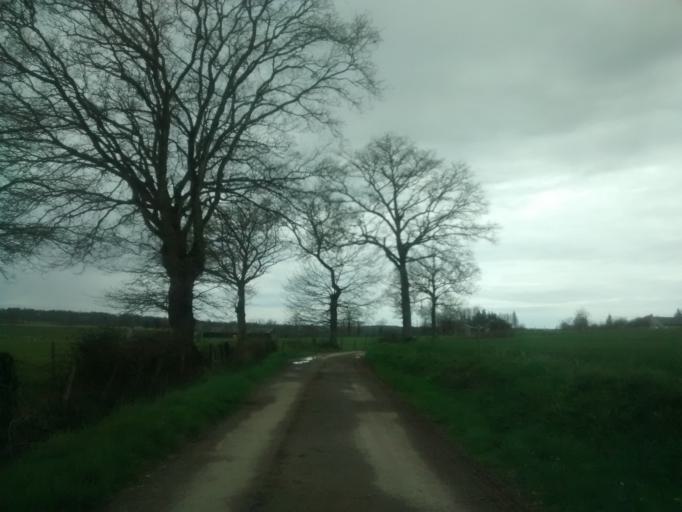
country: FR
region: Brittany
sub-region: Departement d'Ille-et-Vilaine
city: Gosne
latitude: 48.2420
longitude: -1.4705
